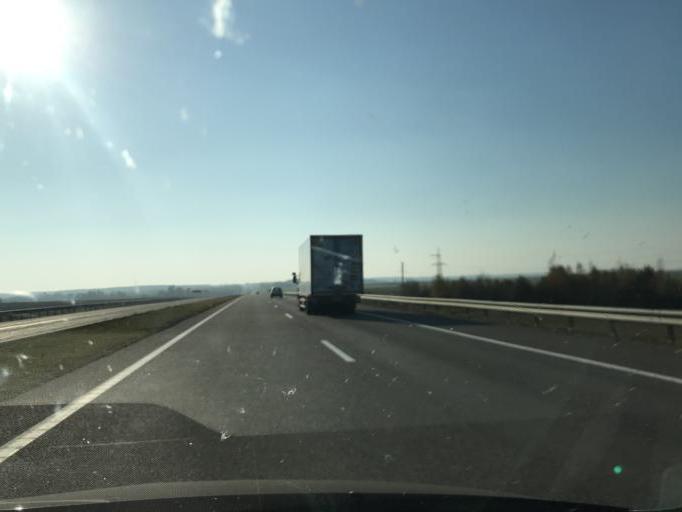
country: BY
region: Minsk
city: Haradzyeya
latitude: 53.3979
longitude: 26.5398
